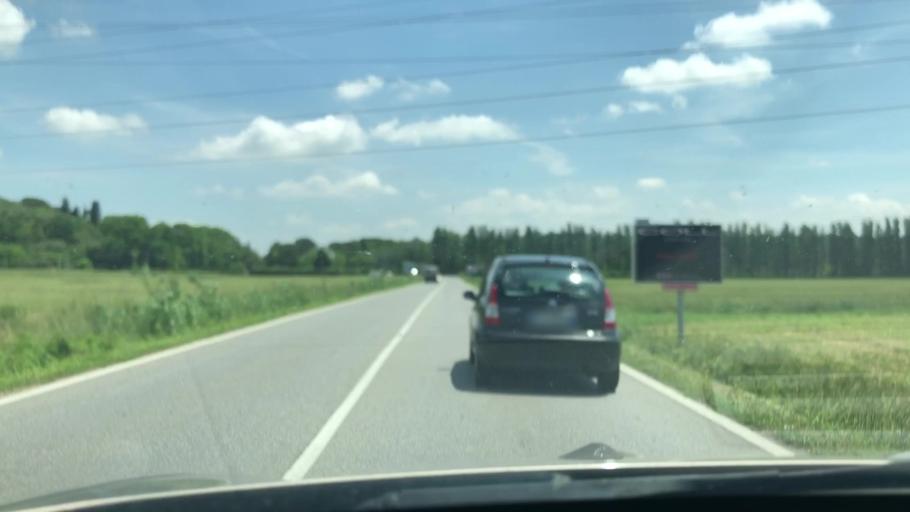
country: IT
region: Tuscany
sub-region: Province of Pisa
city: Treggiaia
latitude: 43.6174
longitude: 10.6760
